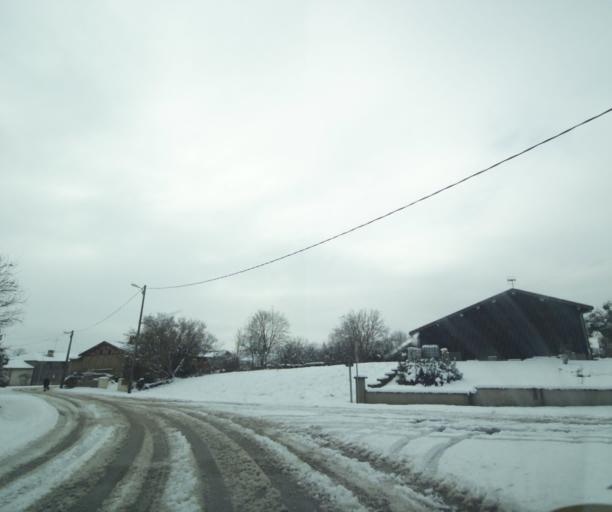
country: FR
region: Champagne-Ardenne
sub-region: Departement de la Haute-Marne
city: Montier-en-Der
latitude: 48.5172
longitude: 4.6994
